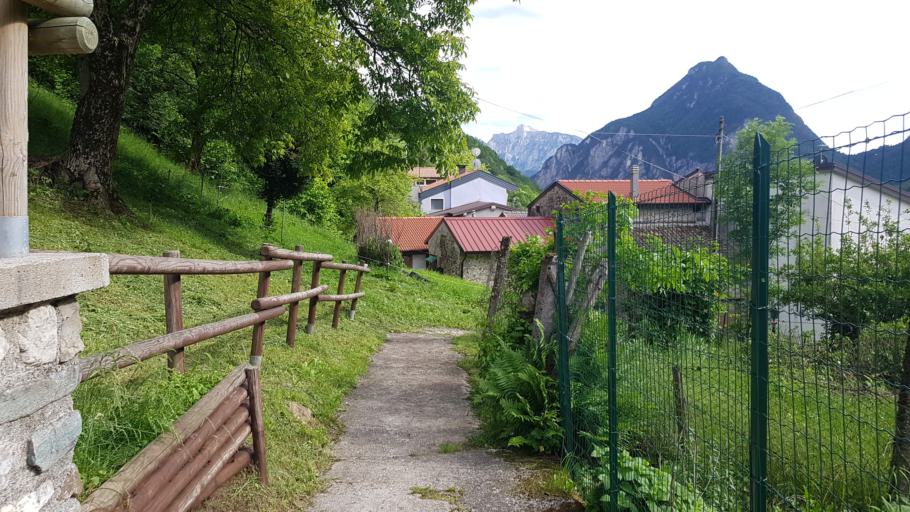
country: IT
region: Friuli Venezia Giulia
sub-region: Provincia di Udine
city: Moggio Udinese
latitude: 46.4689
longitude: 13.1936
